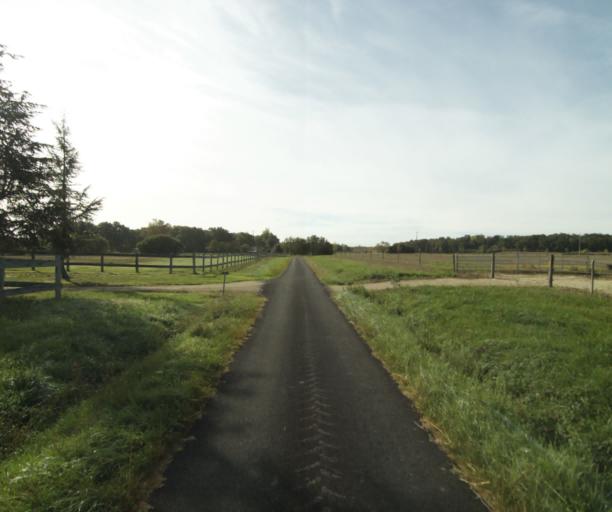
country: FR
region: Midi-Pyrenees
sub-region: Departement du Gers
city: Montreal
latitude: 43.9410
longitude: 0.1253
